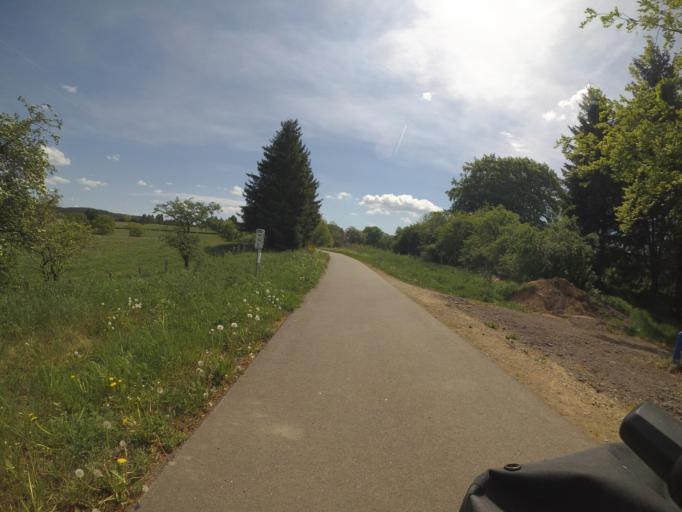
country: BE
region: Wallonia
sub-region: Province de Liege
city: Bullange
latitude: 50.3806
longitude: 6.2900
